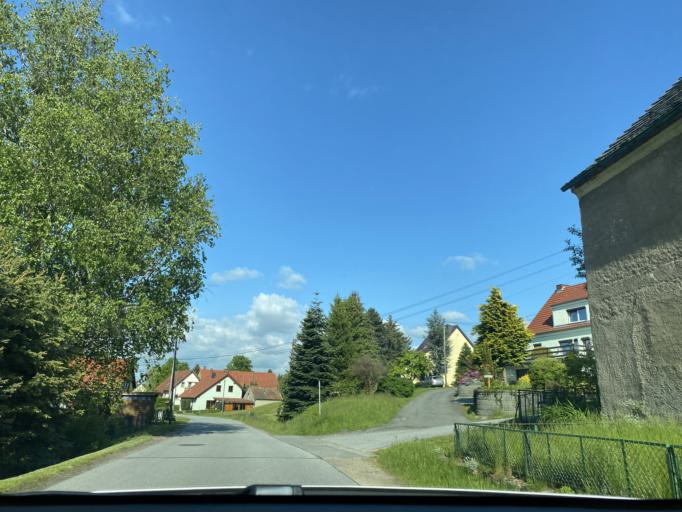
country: DE
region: Saxony
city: Markersdorf
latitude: 51.1193
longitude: 14.8455
